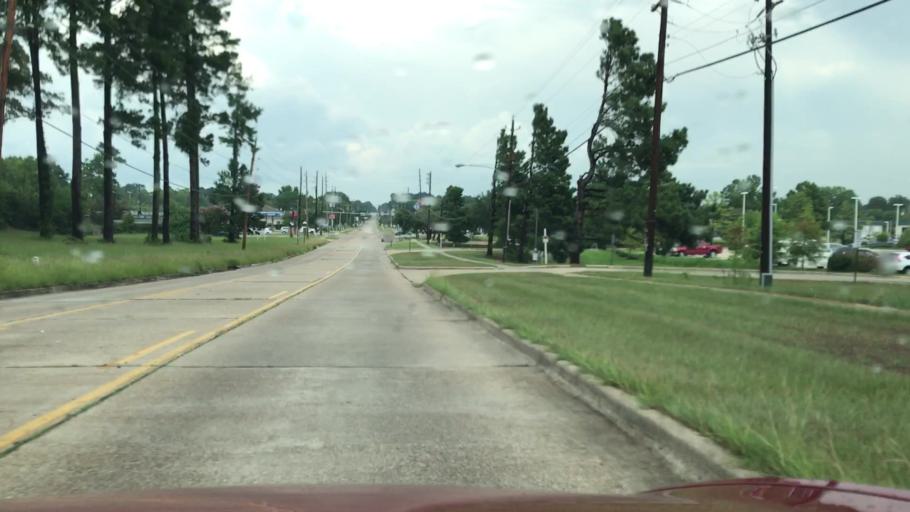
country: US
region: Louisiana
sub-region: De Soto Parish
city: Stonewall
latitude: 32.3994
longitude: -93.7804
